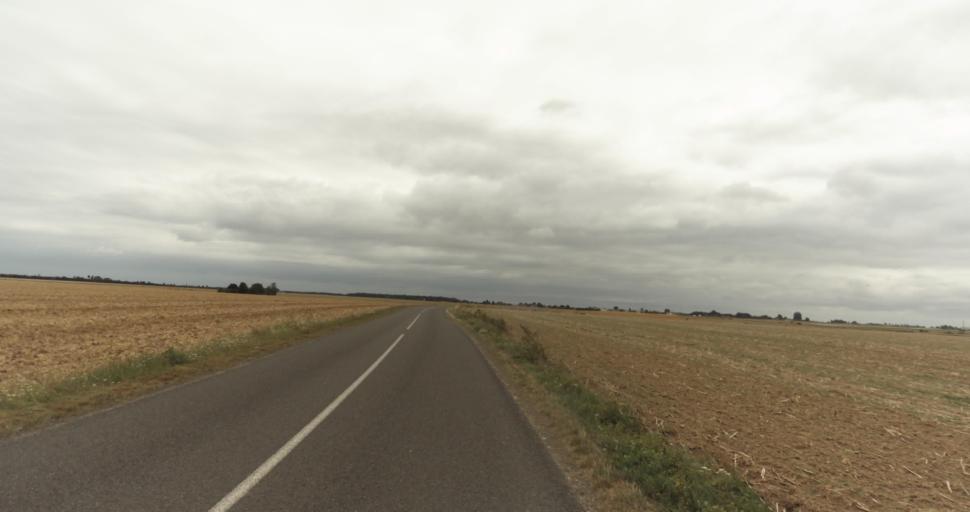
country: FR
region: Haute-Normandie
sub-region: Departement de l'Eure
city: Gravigny
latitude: 49.0440
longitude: 1.2330
